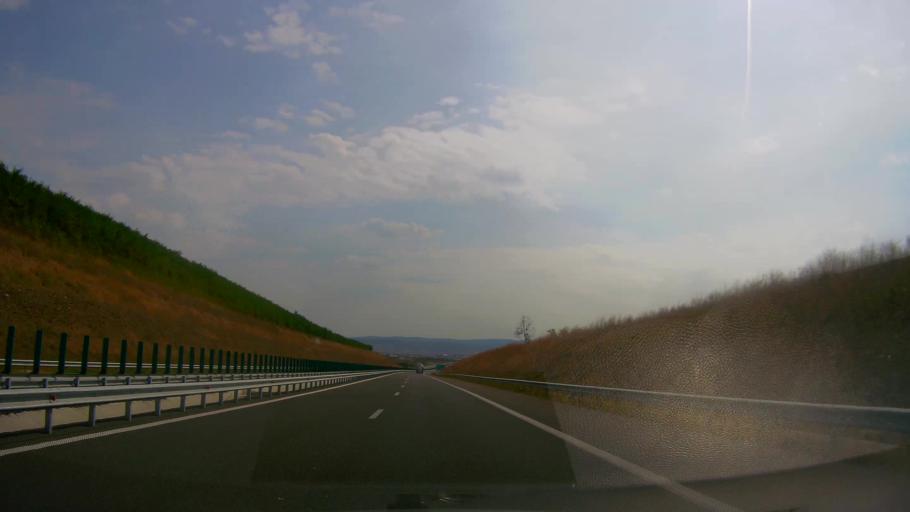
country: RO
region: Cluj
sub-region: Comuna Gilau
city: Gilau
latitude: 46.7621
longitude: 23.3925
